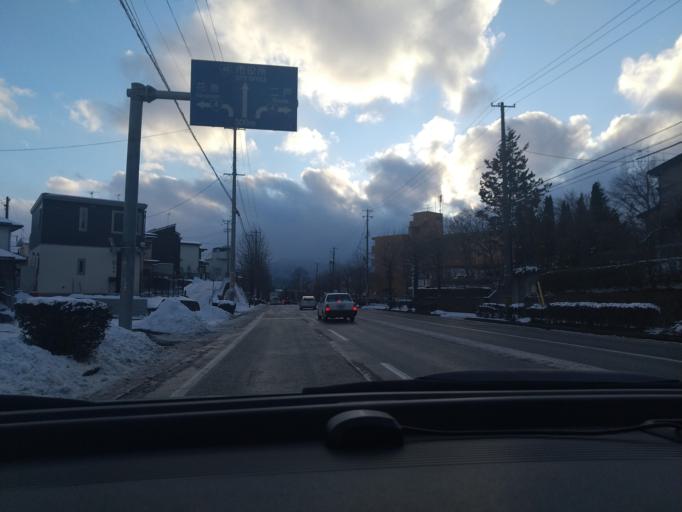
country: JP
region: Iwate
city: Morioka-shi
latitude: 39.7257
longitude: 141.1375
